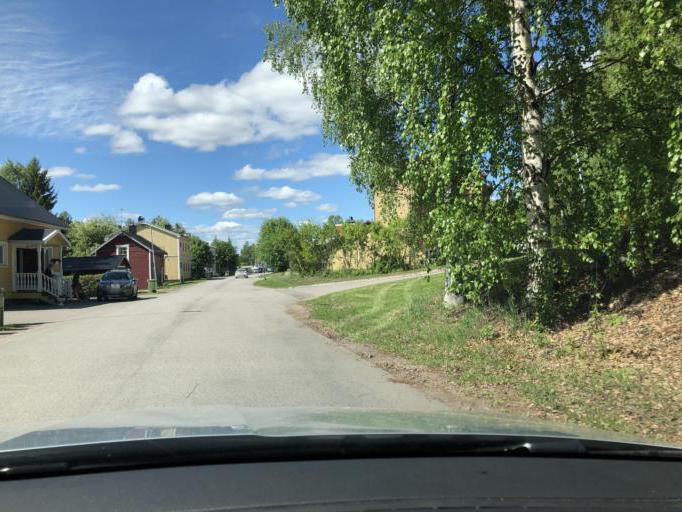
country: SE
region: Norrbotten
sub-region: Alvsbyns Kommun
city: AElvsbyn
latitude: 65.6685
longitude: 21.0154
